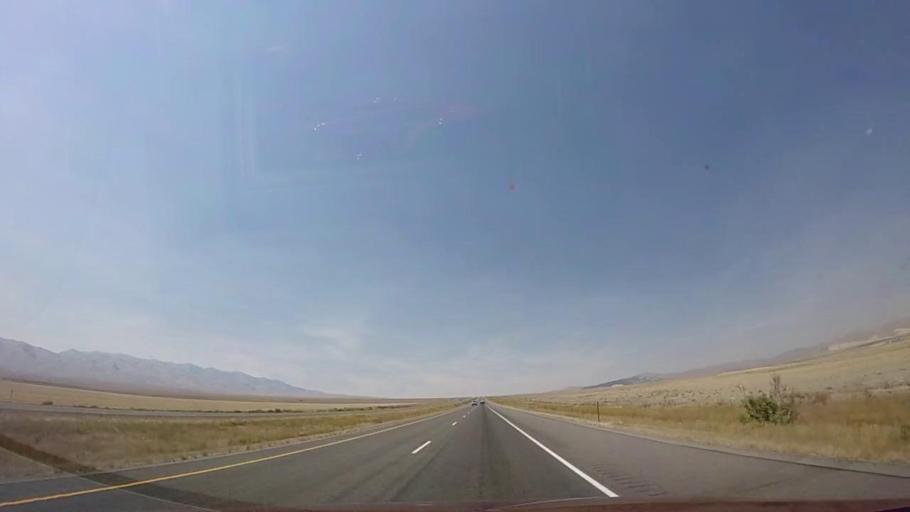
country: US
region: Idaho
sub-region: Power County
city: American Falls
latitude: 42.1146
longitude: -112.9516
